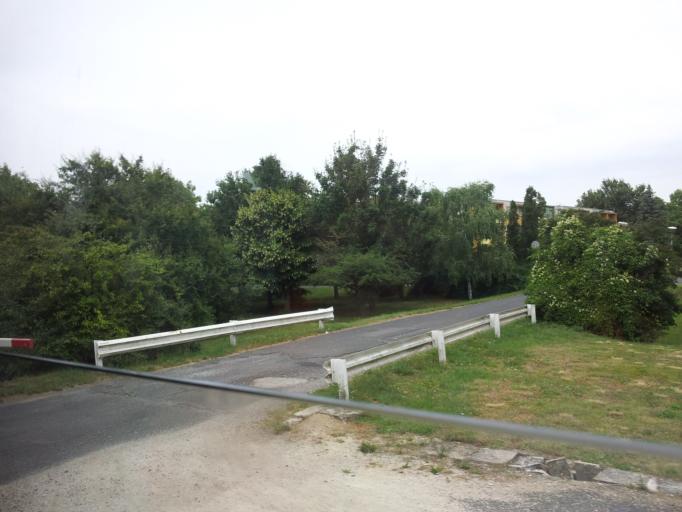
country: HU
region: Veszprem
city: Zanka
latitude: 46.8776
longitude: 17.7082
